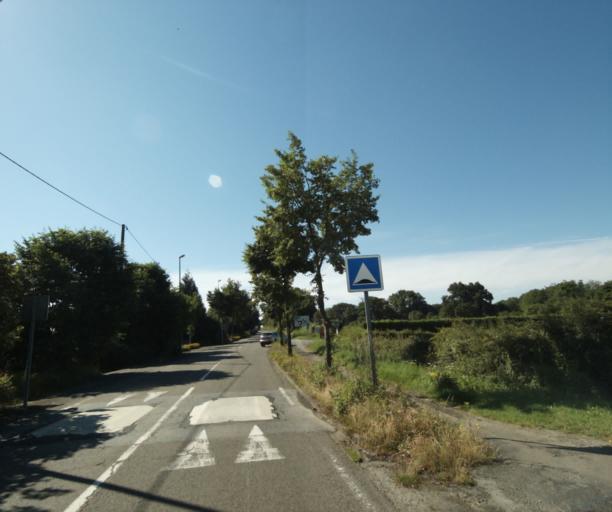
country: FR
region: Pays de la Loire
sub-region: Departement de la Mayenne
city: Laval
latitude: 48.0483
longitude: -0.7454
